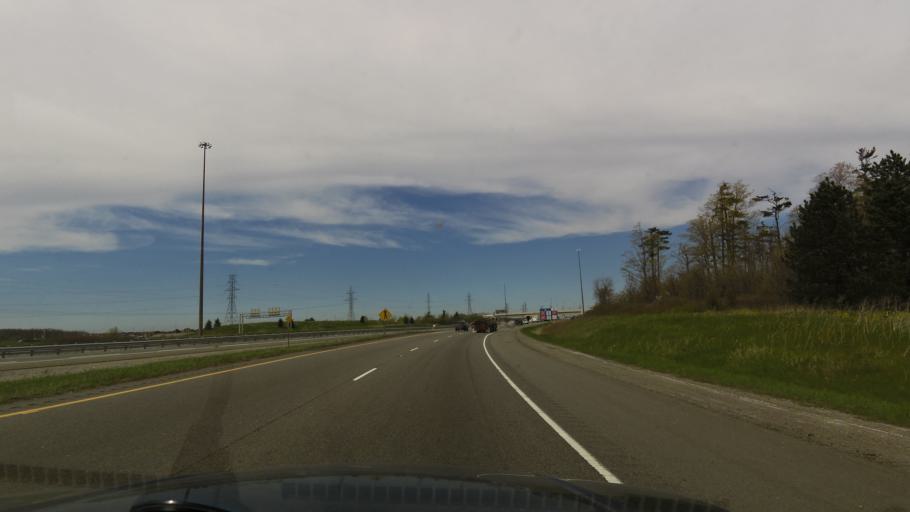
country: CA
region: Ontario
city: Mississauga
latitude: 43.5306
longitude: -79.7221
